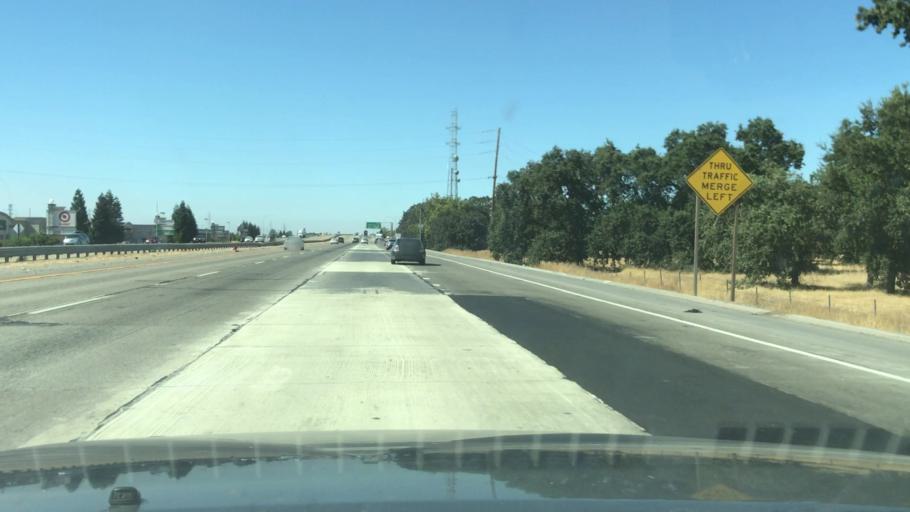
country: US
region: California
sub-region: San Joaquin County
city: Lincoln Village
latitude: 38.0514
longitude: -121.3704
